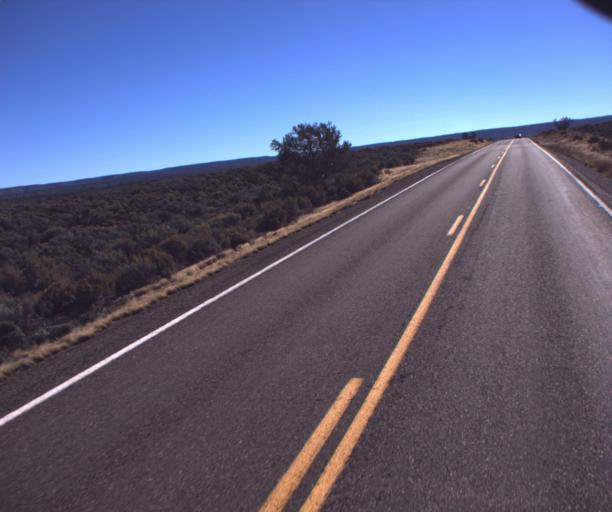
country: US
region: Arizona
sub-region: Coconino County
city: Fredonia
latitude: 36.8732
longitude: -112.3286
